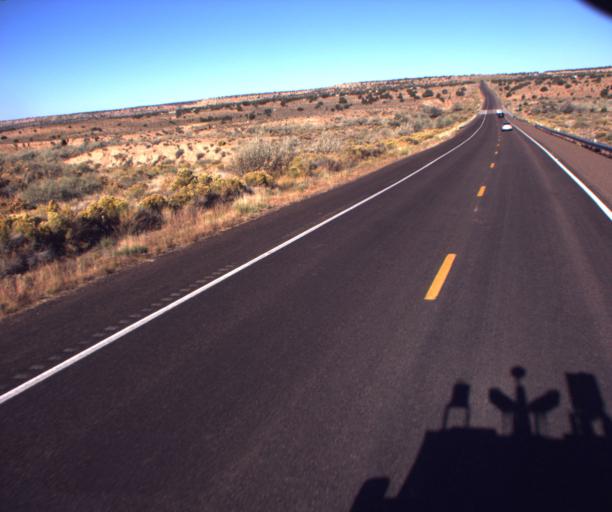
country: US
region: Arizona
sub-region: Navajo County
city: First Mesa
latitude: 35.7551
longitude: -110.1375
